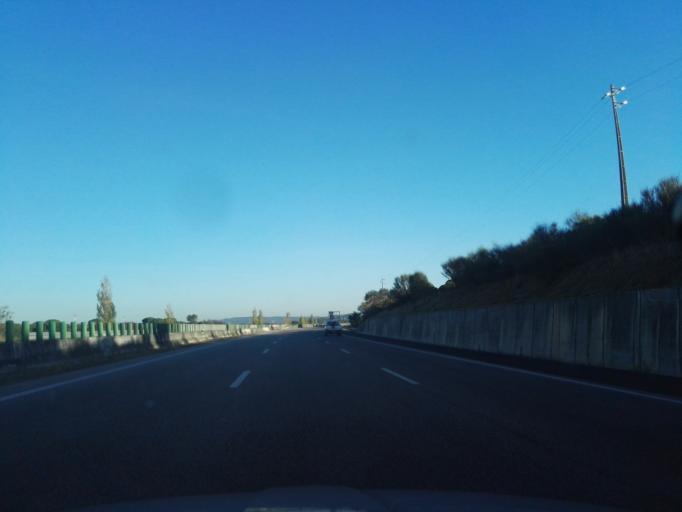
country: PT
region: Lisbon
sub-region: Alenquer
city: Carregado
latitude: 39.0585
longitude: -8.9415
